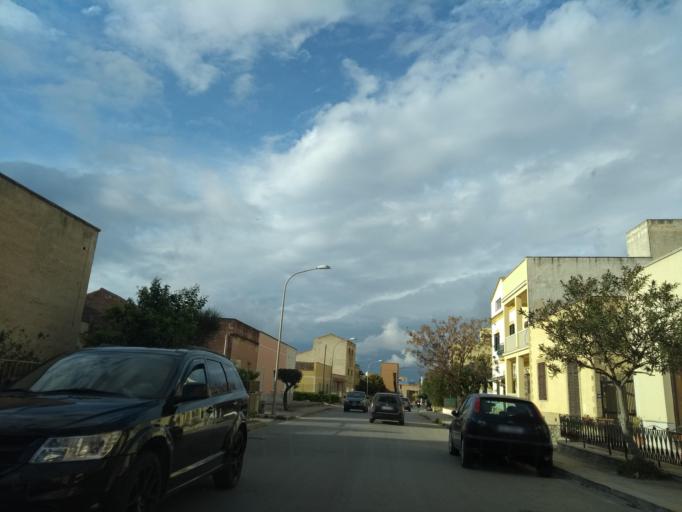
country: IT
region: Sicily
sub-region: Trapani
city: Marausa
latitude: 37.9420
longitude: 12.5105
